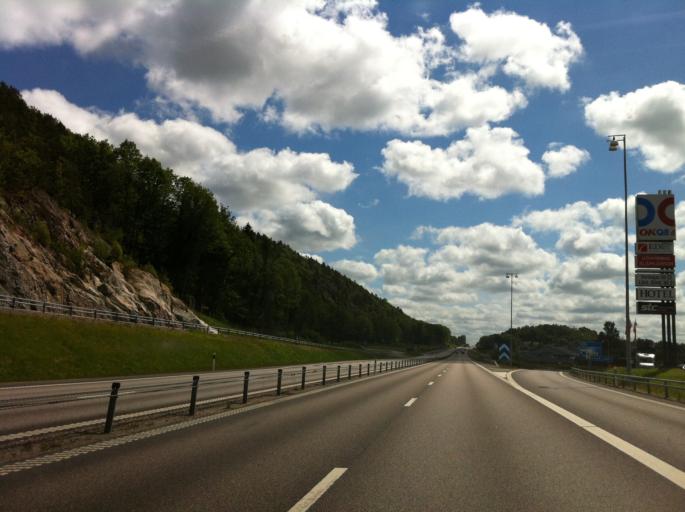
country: SE
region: Vaestra Goetaland
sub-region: Lilla Edets Kommun
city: Lilla Edet
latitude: 58.1497
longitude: 12.1348
